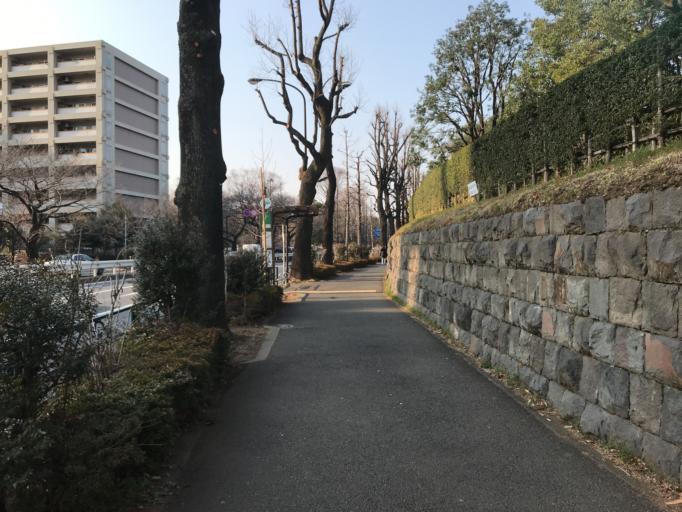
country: JP
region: Tokyo
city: Tokyo
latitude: 35.6749
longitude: 139.7224
